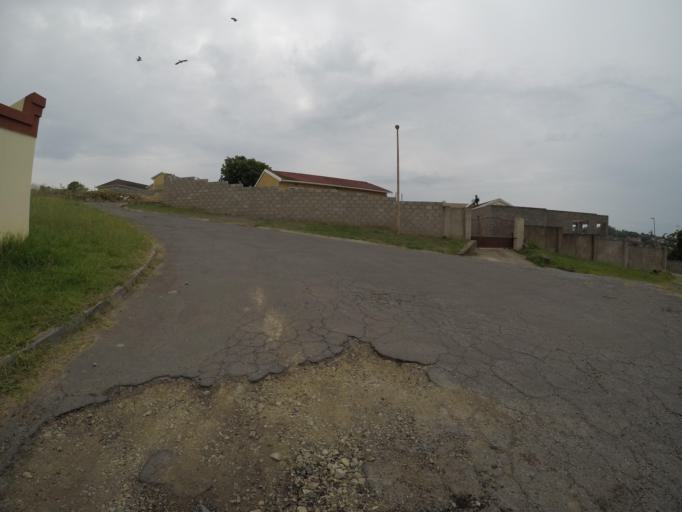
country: ZA
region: Eastern Cape
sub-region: Buffalo City Metropolitan Municipality
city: East London
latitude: -32.9997
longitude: 27.8597
